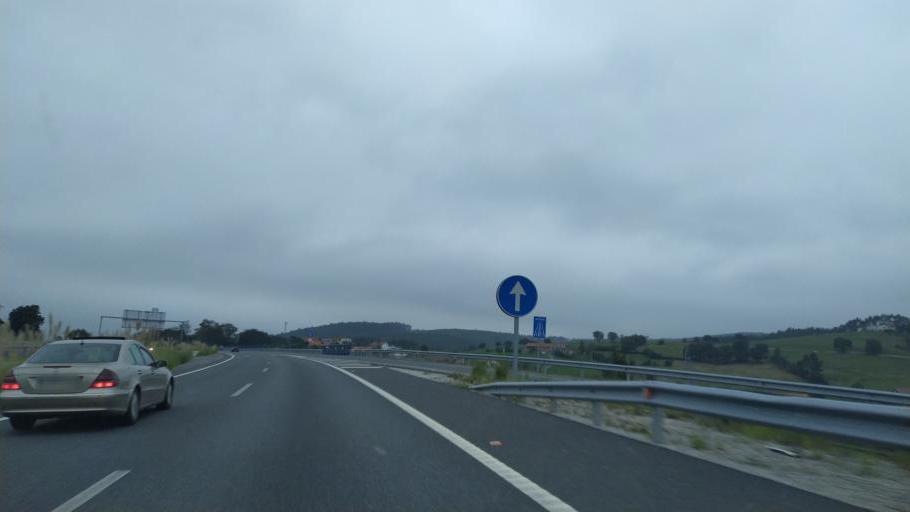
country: ES
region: Cantabria
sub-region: Provincia de Cantabria
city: Polanco
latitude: 43.3440
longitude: -3.9936
